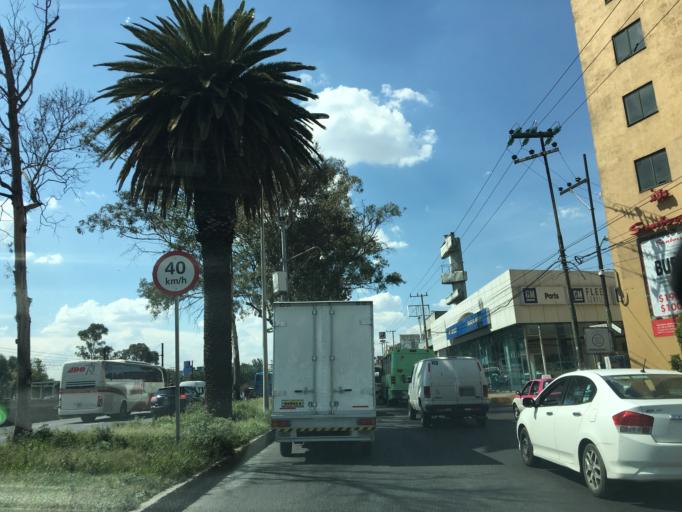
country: MX
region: Mexico City
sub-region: Iztacalco
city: Iztacalco
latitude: 19.4005
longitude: -99.0618
